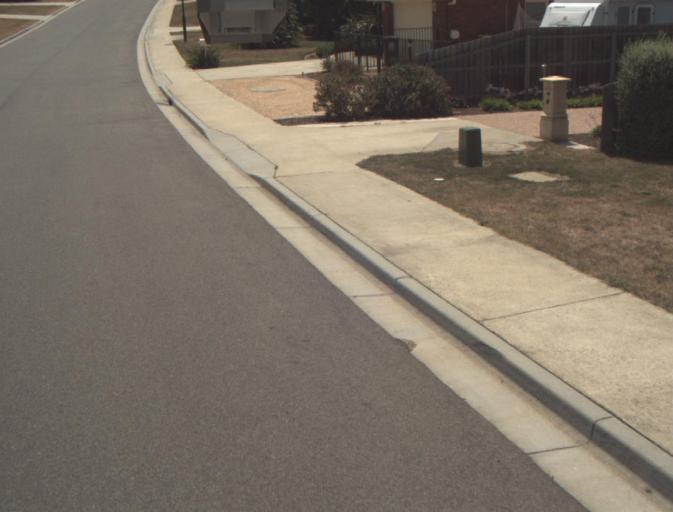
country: AU
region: Tasmania
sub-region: Launceston
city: Newstead
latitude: -41.4832
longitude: 147.1837
